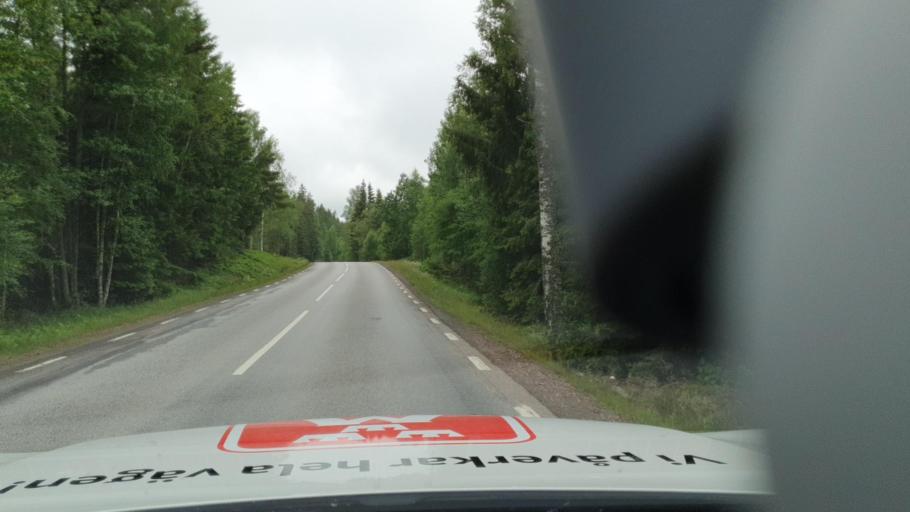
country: SE
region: Vaermland
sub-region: Kristinehamns Kommun
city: Bjorneborg
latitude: 59.1076
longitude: 14.2332
